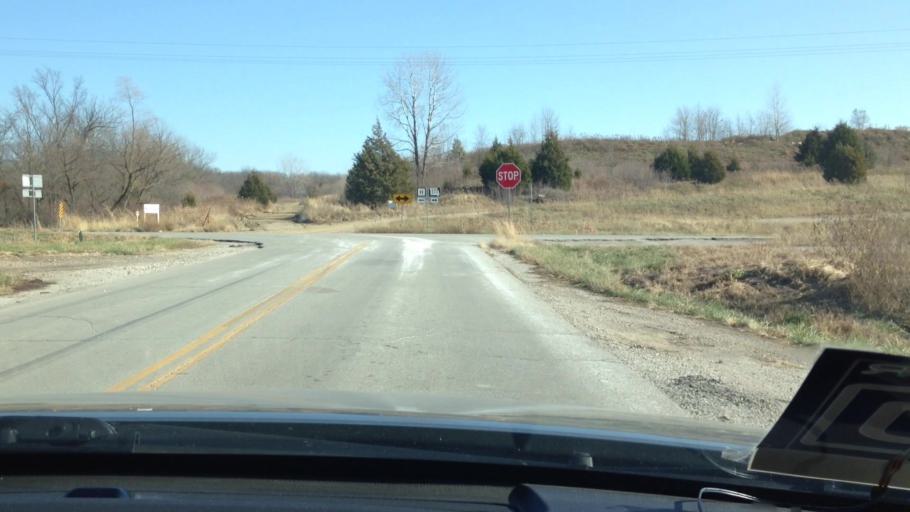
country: US
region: Missouri
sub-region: Platte County
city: Platte City
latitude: 39.4975
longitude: -94.8022
